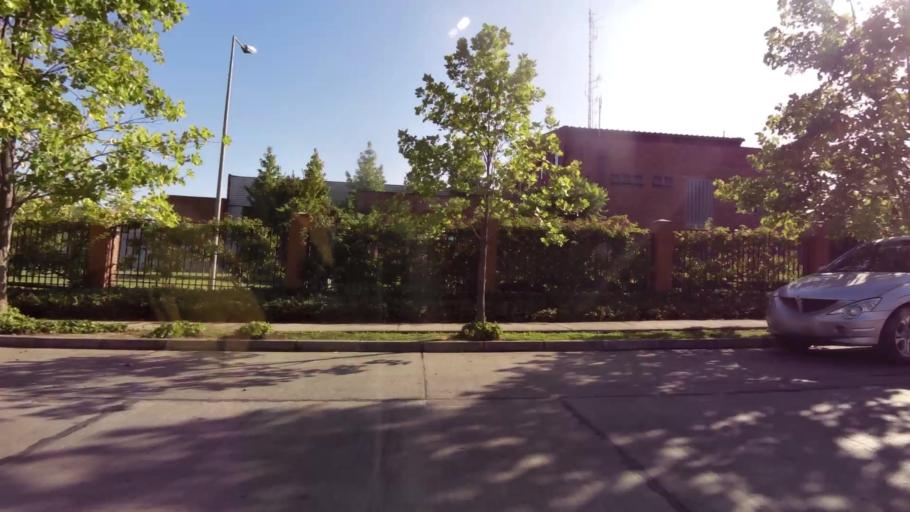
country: CL
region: Maule
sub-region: Provincia de Talca
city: Talca
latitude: -35.4194
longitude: -71.6717
